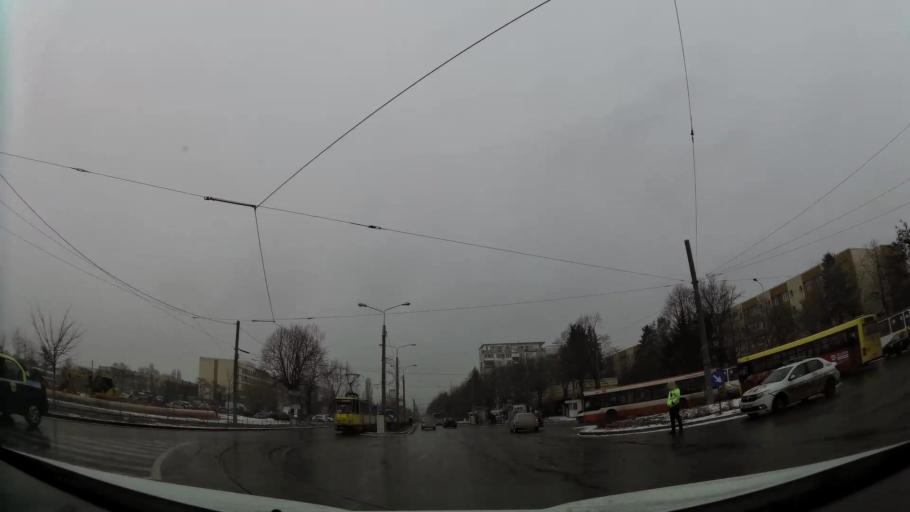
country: RO
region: Prahova
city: Ploiesti
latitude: 44.9636
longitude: 26.0067
